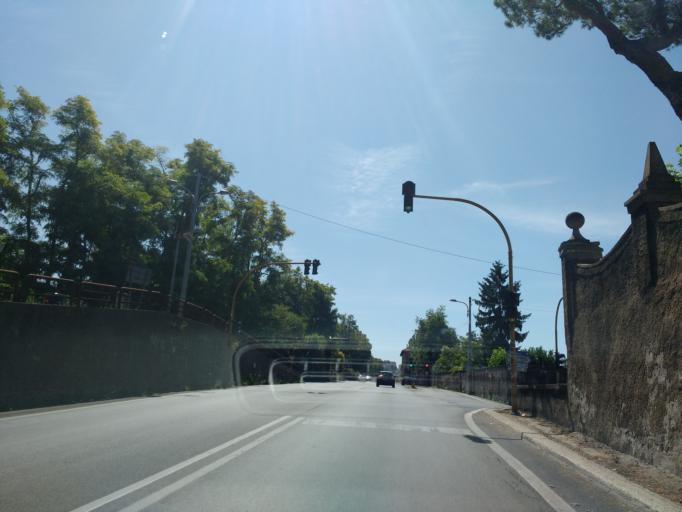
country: IT
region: Latium
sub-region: Citta metropolitana di Roma Capitale
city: Castel Gandolfo
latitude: 41.7427
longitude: 12.6430
